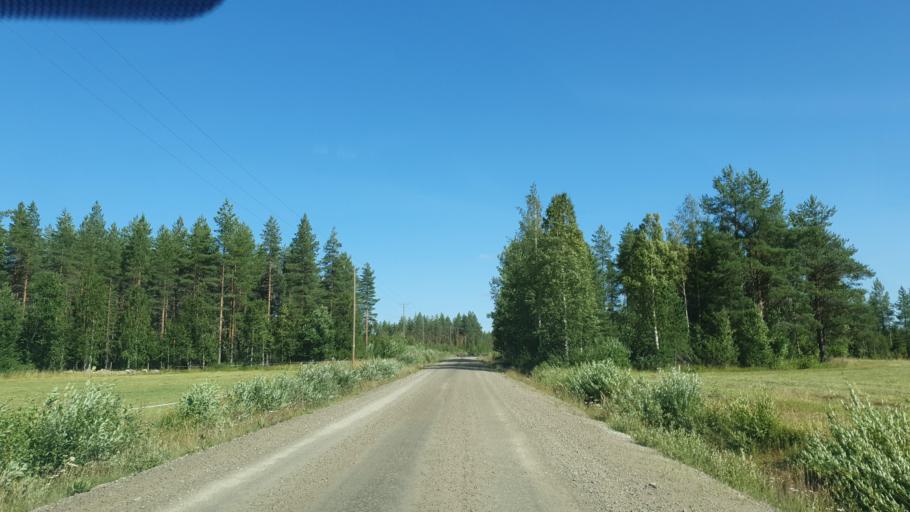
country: FI
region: Kainuu
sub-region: Kehys-Kainuu
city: Kuhmo
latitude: 64.0519
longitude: 29.5955
